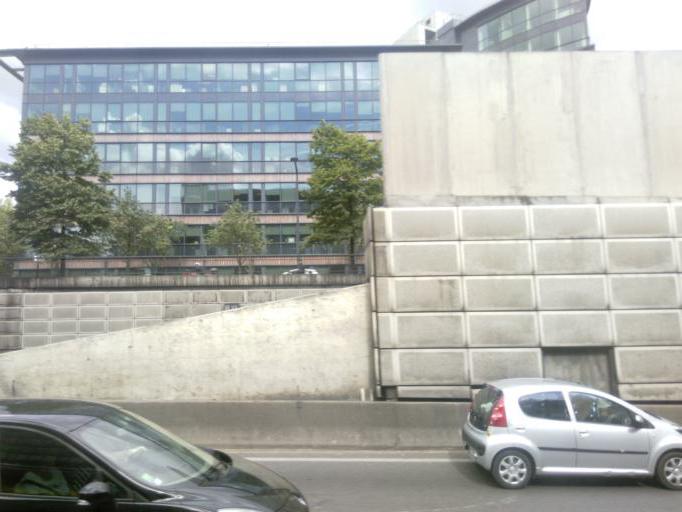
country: FR
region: Ile-de-France
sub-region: Departement de Seine-Saint-Denis
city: Saint-Denis
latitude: 48.9186
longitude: 2.3574
